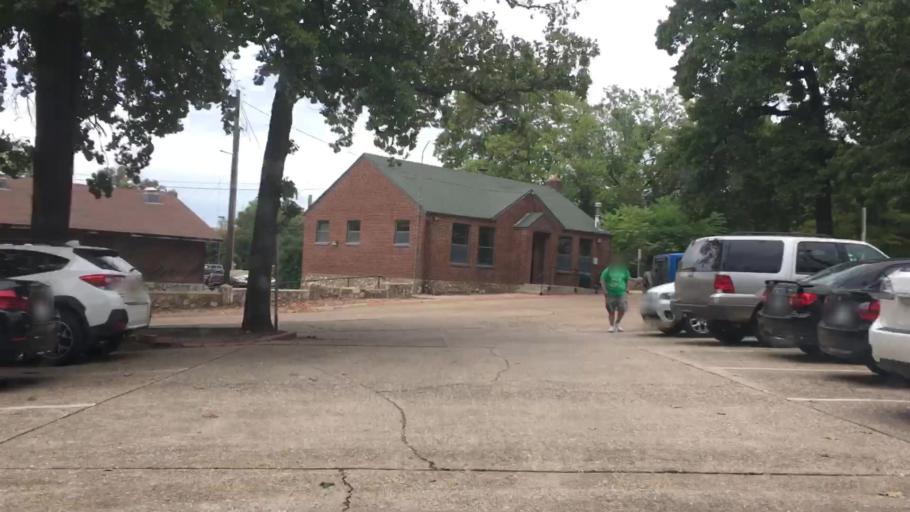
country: US
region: Oklahoma
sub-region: Cherokee County
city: Tahlequah
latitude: 35.9209
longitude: -94.9705
